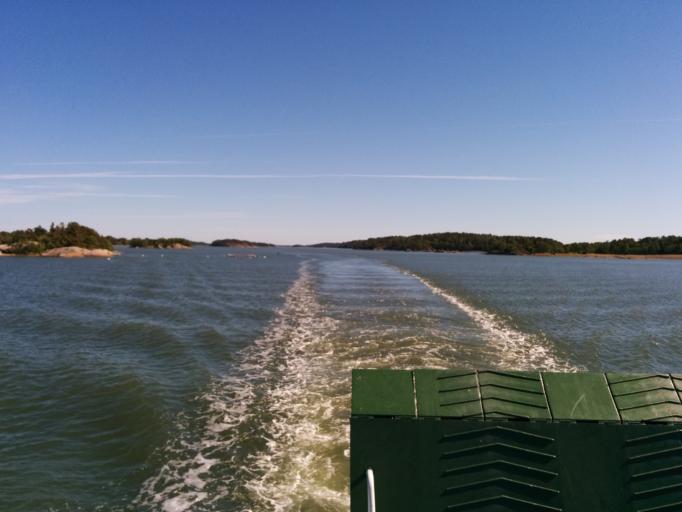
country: FI
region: Varsinais-Suomi
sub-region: Turku
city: Velkua
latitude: 60.4587
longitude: 21.6999
